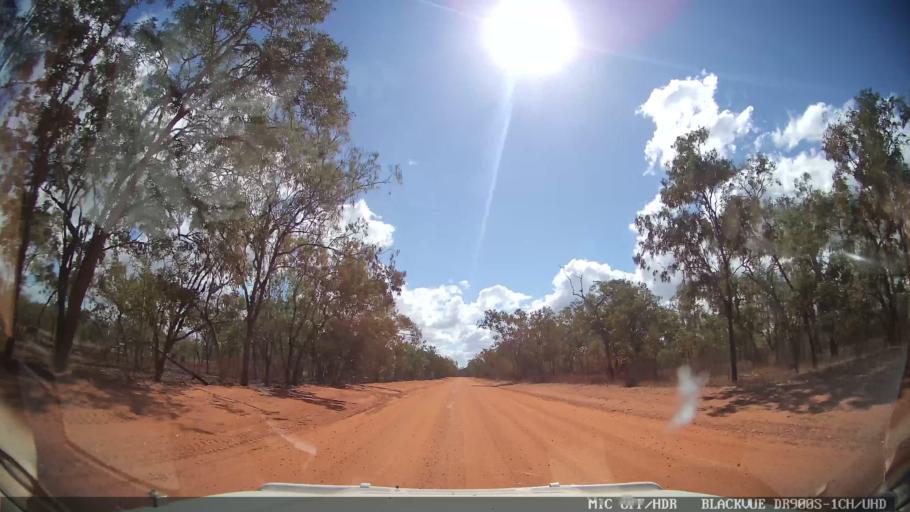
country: AU
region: Queensland
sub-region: Cook
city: Cooktown
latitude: -15.1953
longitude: 144.3794
